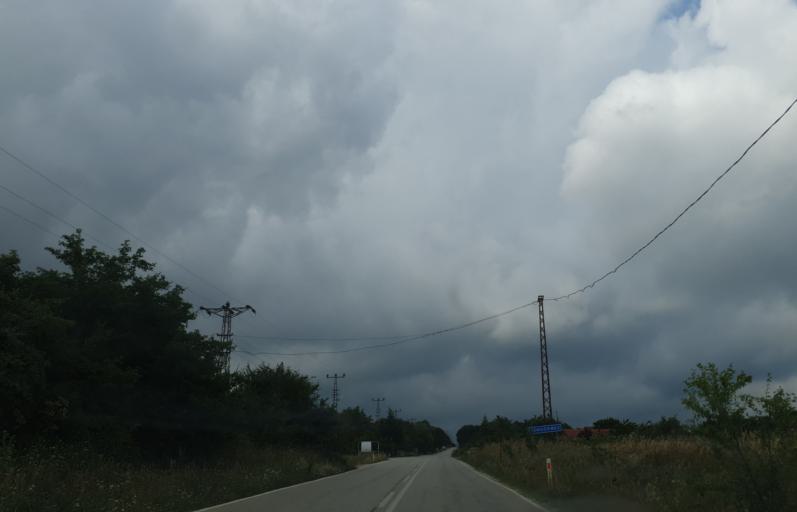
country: TR
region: Tekirdag
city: Saray
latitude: 41.4893
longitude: 27.9712
